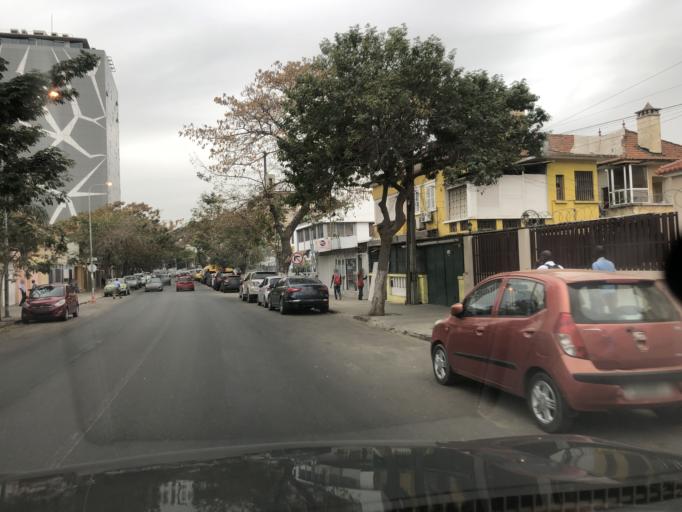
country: AO
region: Luanda
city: Luanda
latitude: -8.8258
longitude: 13.2364
